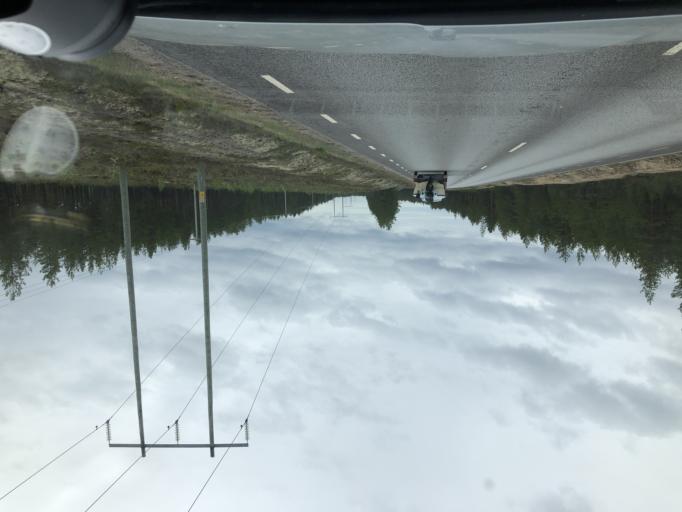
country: SE
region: Norrbotten
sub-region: Pitea Kommun
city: Pitea
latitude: 65.2599
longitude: 21.5384
